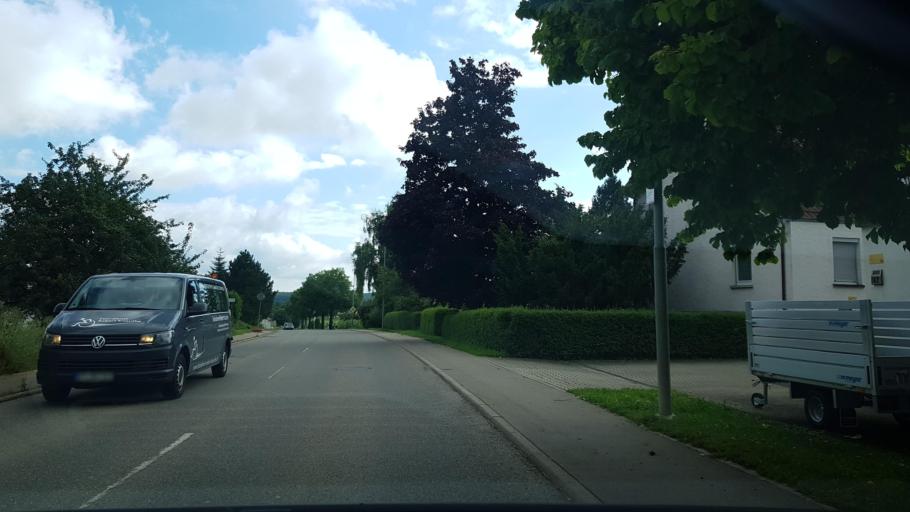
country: DE
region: Baden-Wuerttemberg
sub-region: Tuebingen Region
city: Grabenstetten
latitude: 48.5206
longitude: 9.4613
